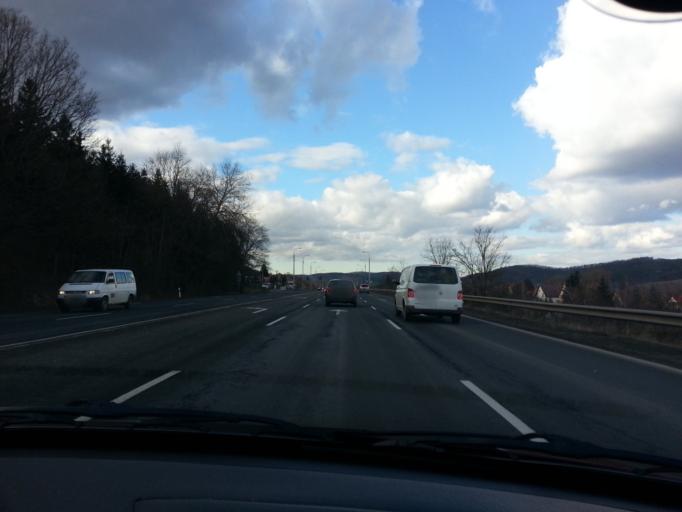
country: HU
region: Nograd
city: Kazar
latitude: 48.0325
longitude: 19.8070
